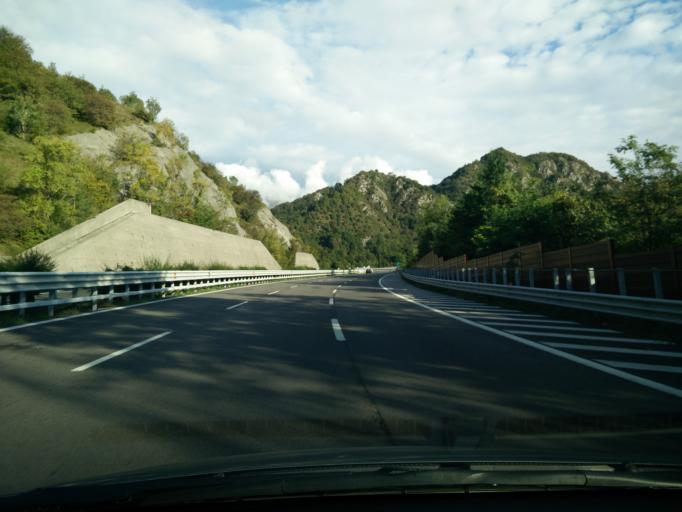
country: IT
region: Veneto
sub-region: Provincia di Treviso
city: Carpesica
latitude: 45.9746
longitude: 12.2830
